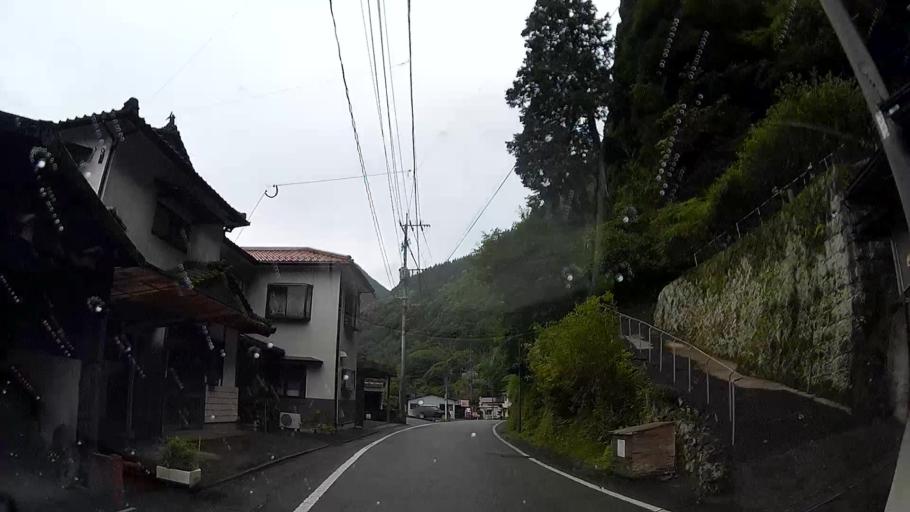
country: JP
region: Oita
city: Tsukawaki
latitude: 33.1799
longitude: 131.0372
